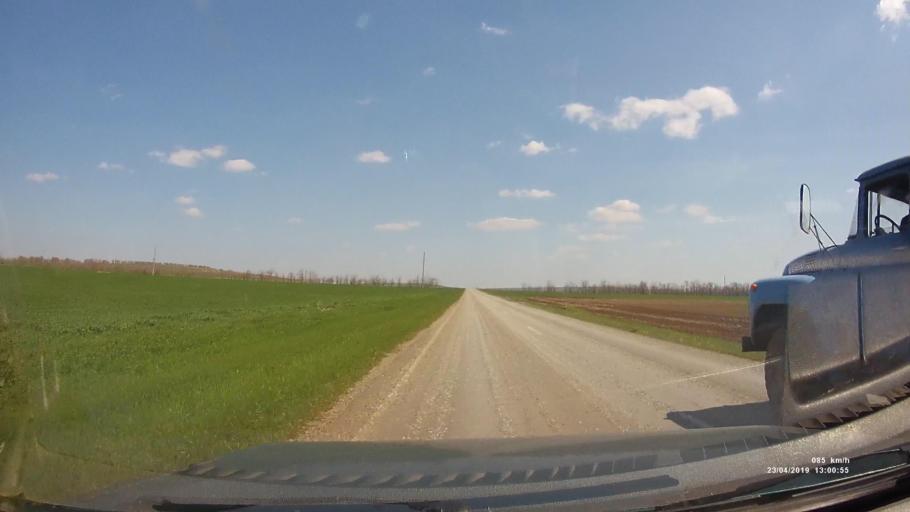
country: RU
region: Kalmykiya
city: Yashalta
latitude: 46.6039
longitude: 42.6429
